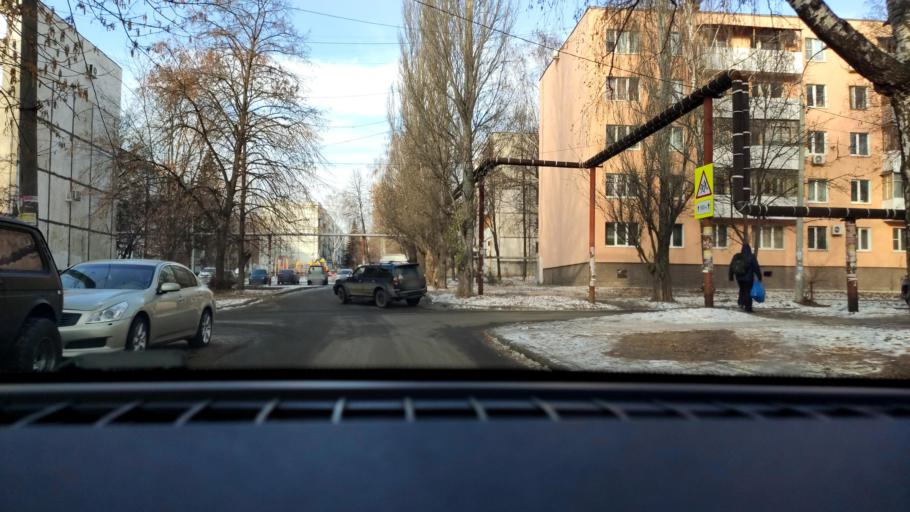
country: RU
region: Samara
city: Petra-Dubrava
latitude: 53.3020
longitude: 50.2711
